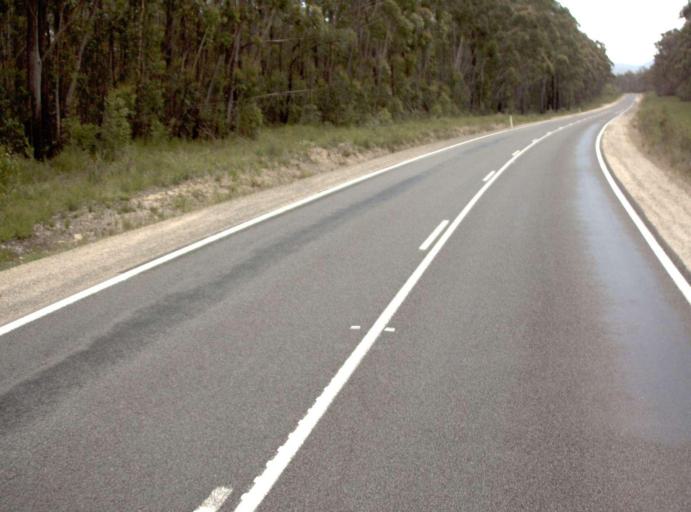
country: AU
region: New South Wales
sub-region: Bega Valley
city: Eden
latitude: -37.5376
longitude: 149.4735
